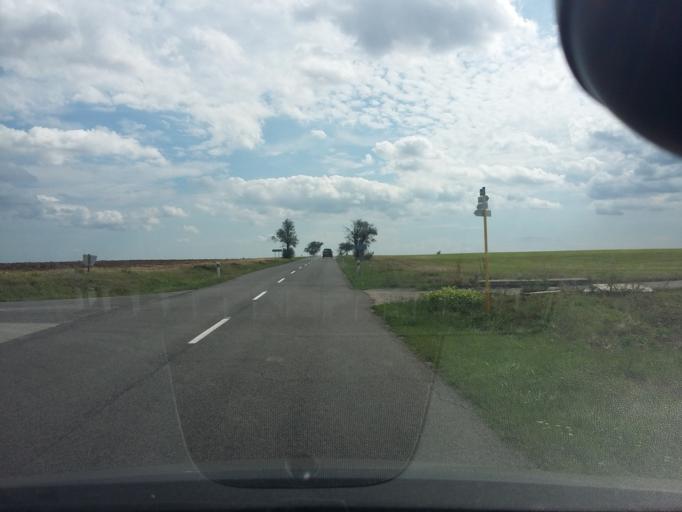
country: SK
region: Trnavsky
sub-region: Okres Skalica
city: Holic
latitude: 48.7589
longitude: 17.1721
